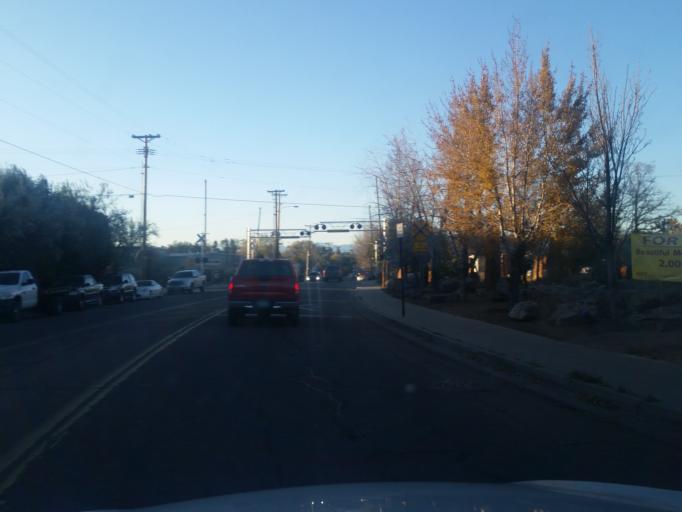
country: US
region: New Mexico
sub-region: Santa Fe County
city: Santa Fe
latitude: 35.6617
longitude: -105.9641
